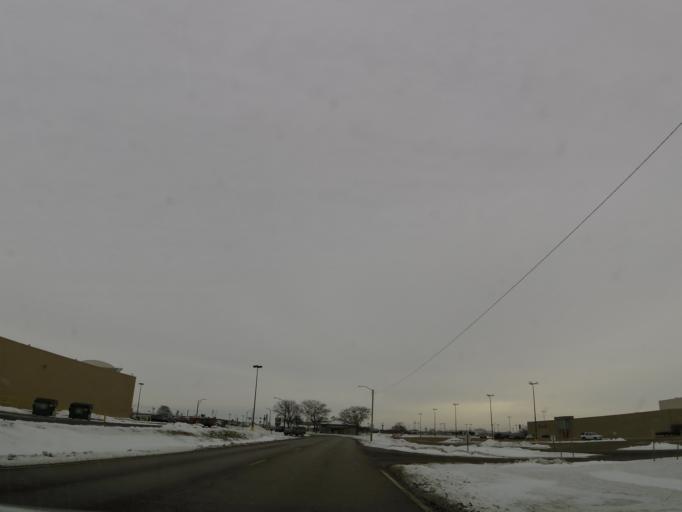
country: US
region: Illinois
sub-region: LaSalle County
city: Peru
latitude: 41.3581
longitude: -89.1299
